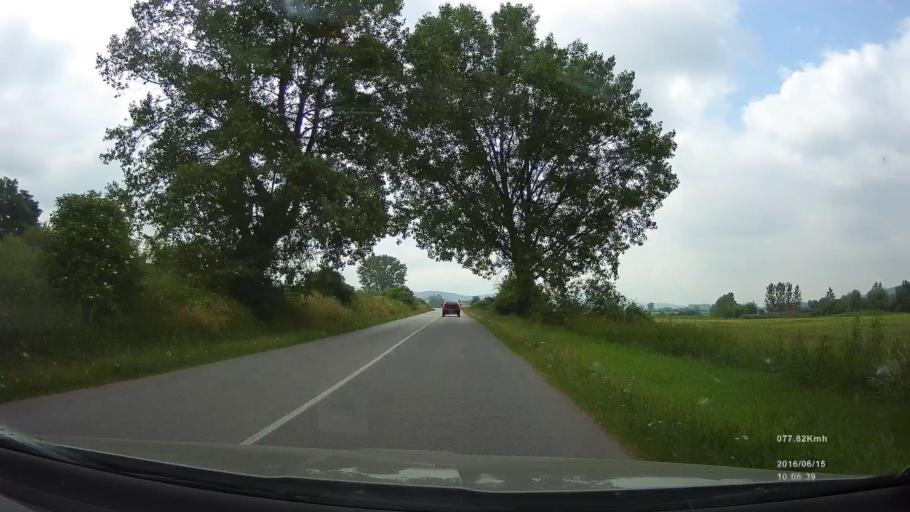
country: SK
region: Kosicky
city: Kosice
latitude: 48.7647
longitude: 21.3322
